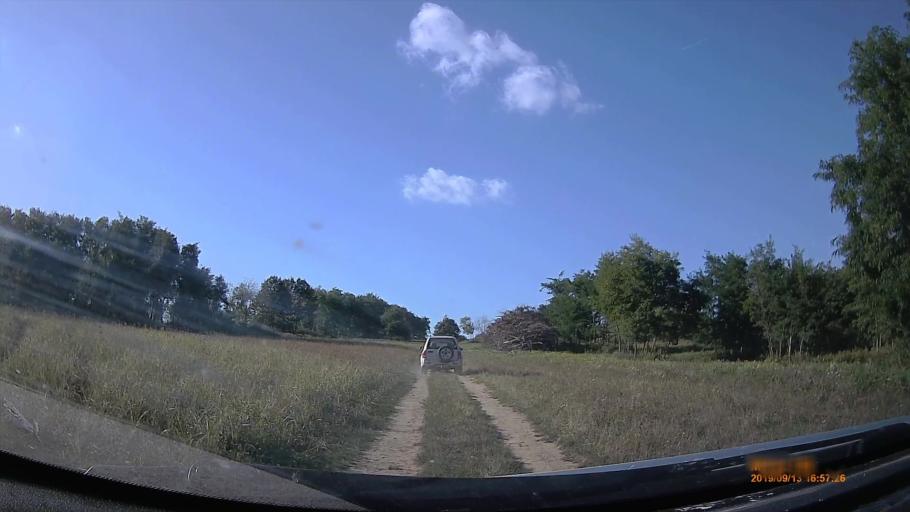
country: HU
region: Zala
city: Pacsa
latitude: 46.5990
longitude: 17.0514
